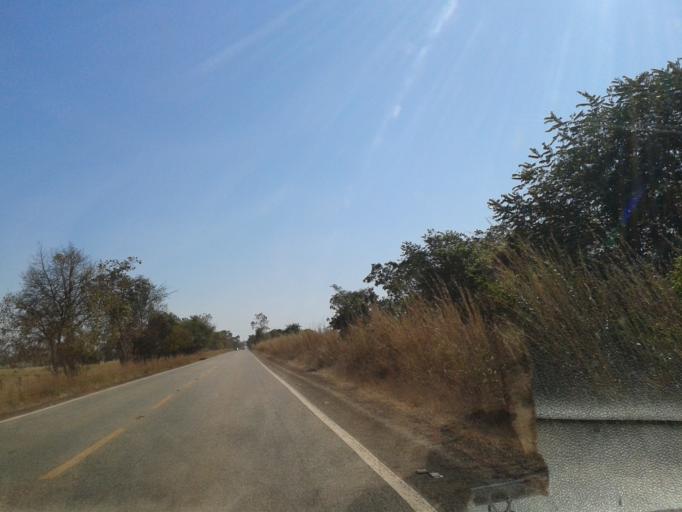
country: BR
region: Goias
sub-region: Mozarlandia
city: Mozarlandia
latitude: -14.3034
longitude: -50.4040
